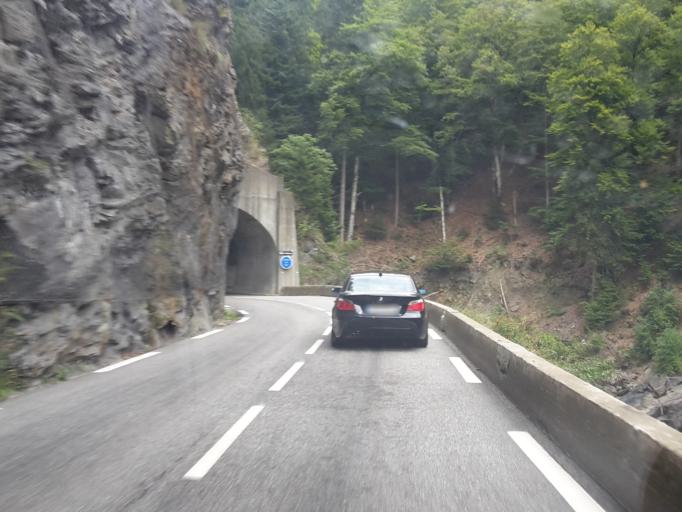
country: FR
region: Rhone-Alpes
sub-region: Departement de la Savoie
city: Ugine
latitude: 45.7899
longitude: 6.4865
